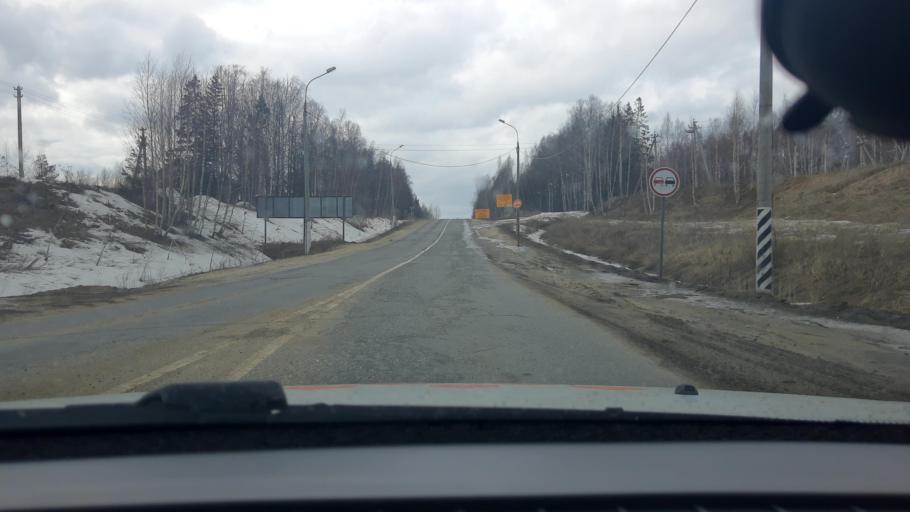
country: RU
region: Nizjnij Novgorod
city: Pervomayskiy
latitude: 56.6318
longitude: 43.2537
